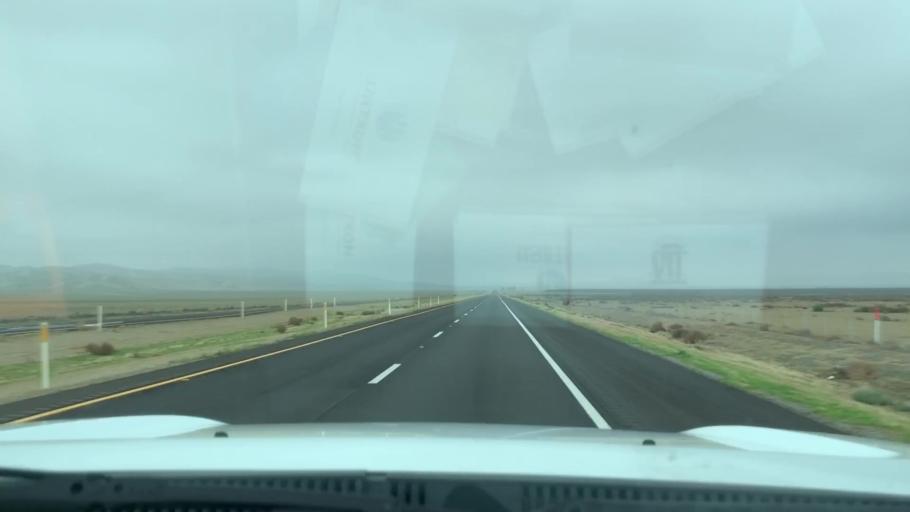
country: US
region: California
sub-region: Kern County
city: Lost Hills
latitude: 35.6203
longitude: -119.9763
